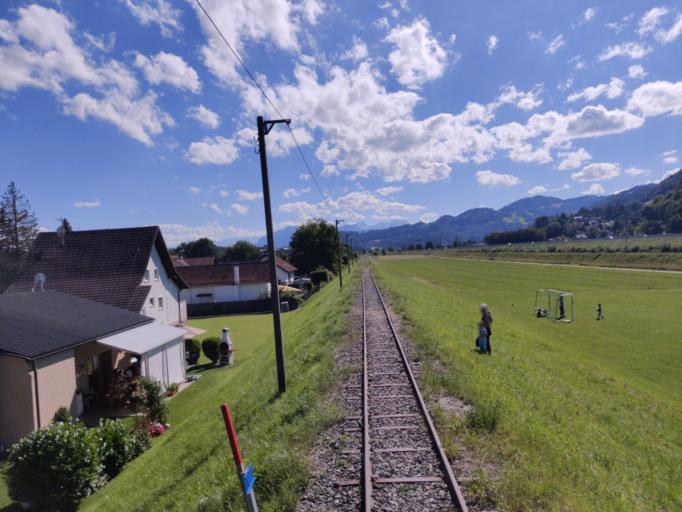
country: AT
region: Vorarlberg
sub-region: Politischer Bezirk Dornbirn
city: Lustenau
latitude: 47.4435
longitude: 9.6542
